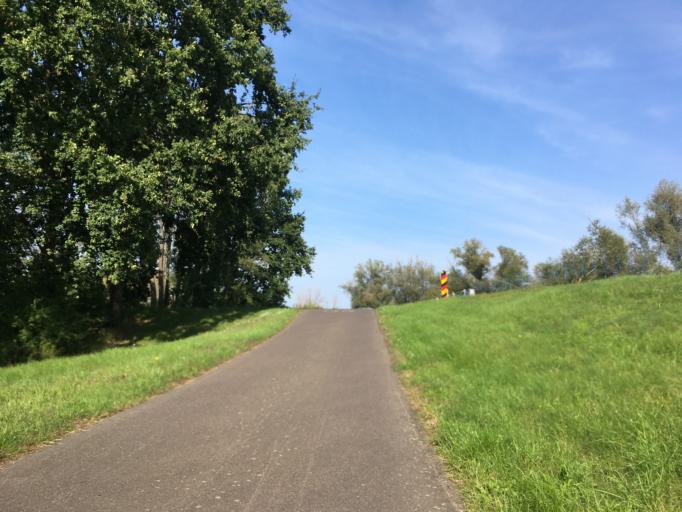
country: DE
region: Brandenburg
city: Vogelsang
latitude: 52.1658
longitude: 14.7015
